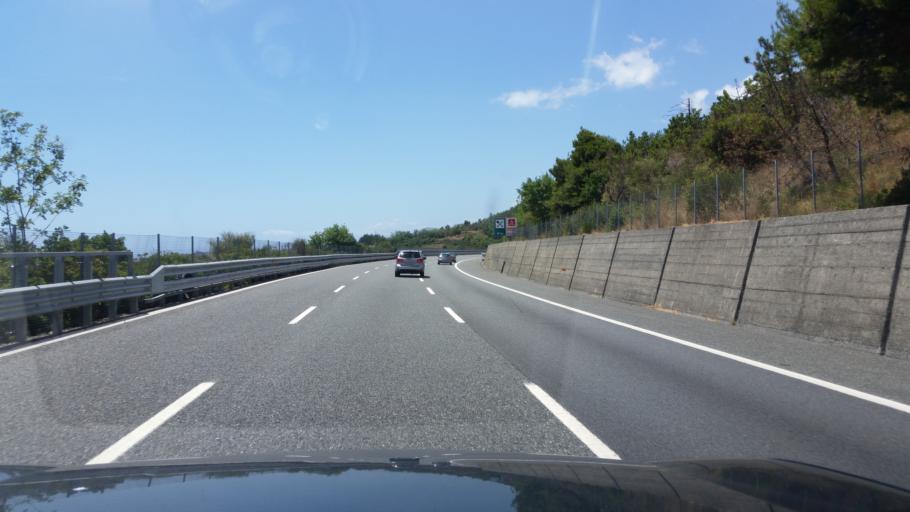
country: IT
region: Liguria
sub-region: Provincia di Genova
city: Arenzano
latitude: 44.4171
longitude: 8.7084
